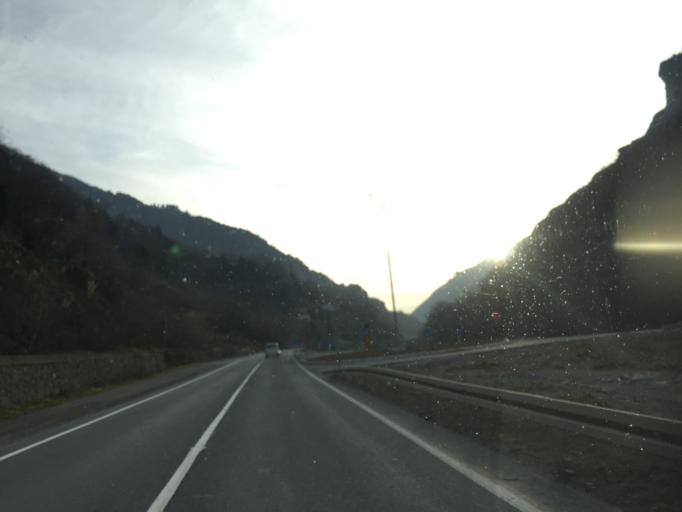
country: TR
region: Trabzon
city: Macka
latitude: 40.7468
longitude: 39.5610
